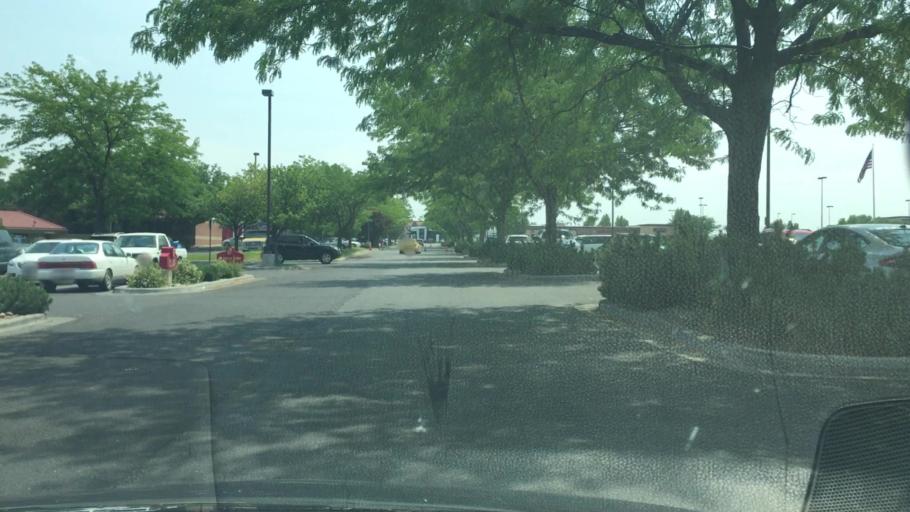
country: US
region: Idaho
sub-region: Twin Falls County
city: Twin Falls
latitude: 42.5913
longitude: -114.4612
